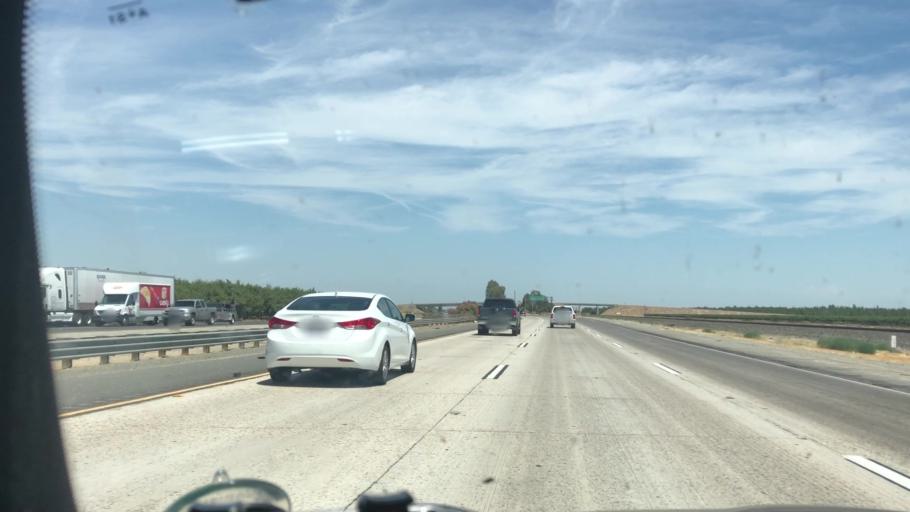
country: US
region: California
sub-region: Kern County
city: McFarland
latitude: 35.6392
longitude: -119.2180
